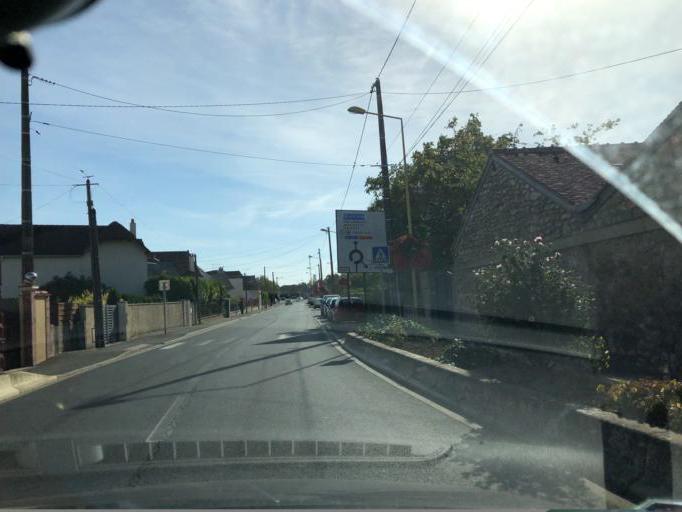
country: FR
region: Centre
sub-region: Departement du Loiret
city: Malesherbes
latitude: 48.2955
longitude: 2.3948
